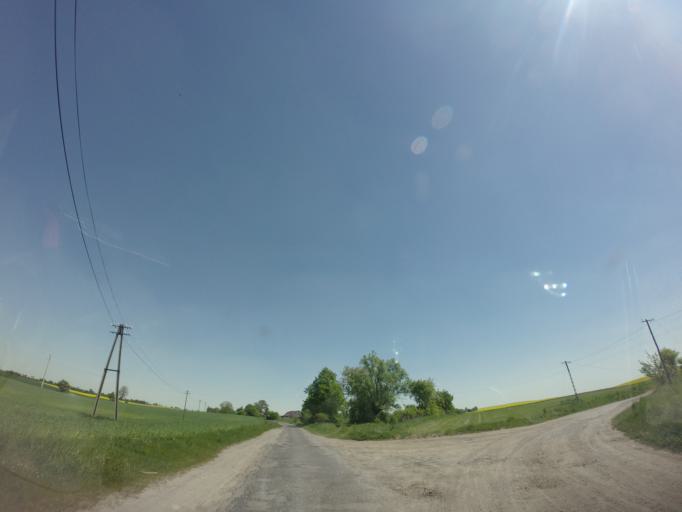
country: PL
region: West Pomeranian Voivodeship
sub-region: Powiat mysliborski
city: Nowogrodek Pomorski
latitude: 52.9084
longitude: 15.0394
